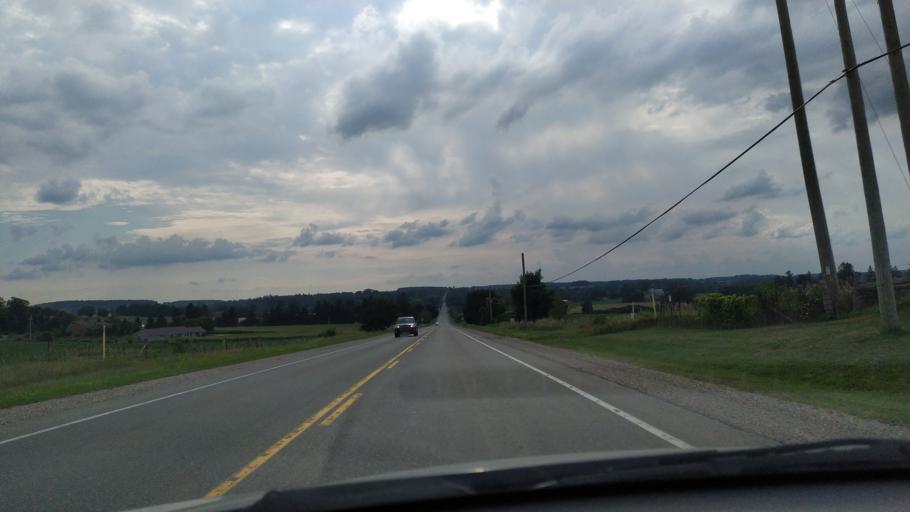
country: CA
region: Ontario
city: Kitchener
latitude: 43.3526
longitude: -80.5138
